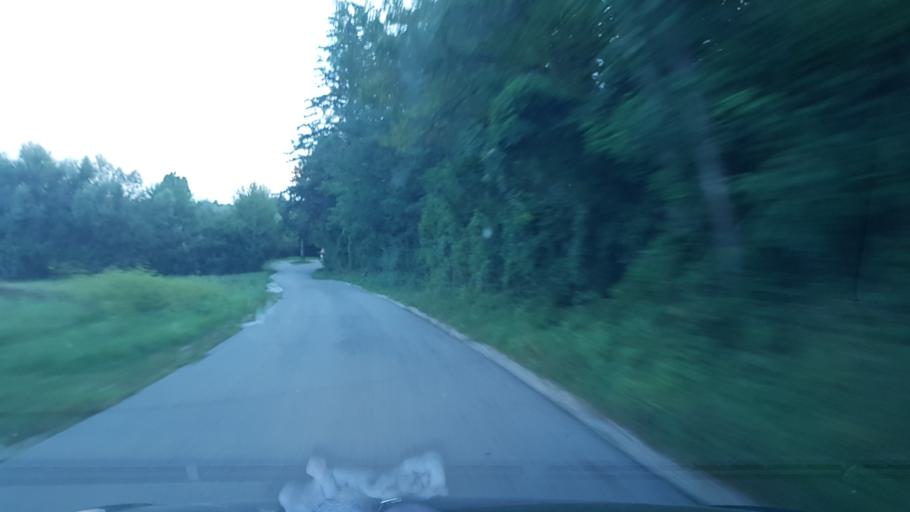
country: SI
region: Postojna
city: Postojna
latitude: 45.7550
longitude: 14.1878
